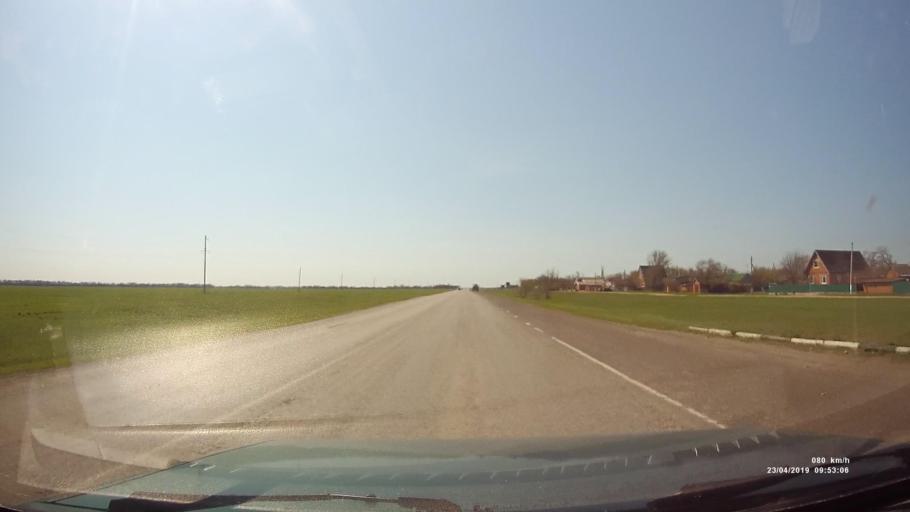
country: RU
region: Rostov
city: Orlovskiy
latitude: 46.8369
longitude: 42.0487
